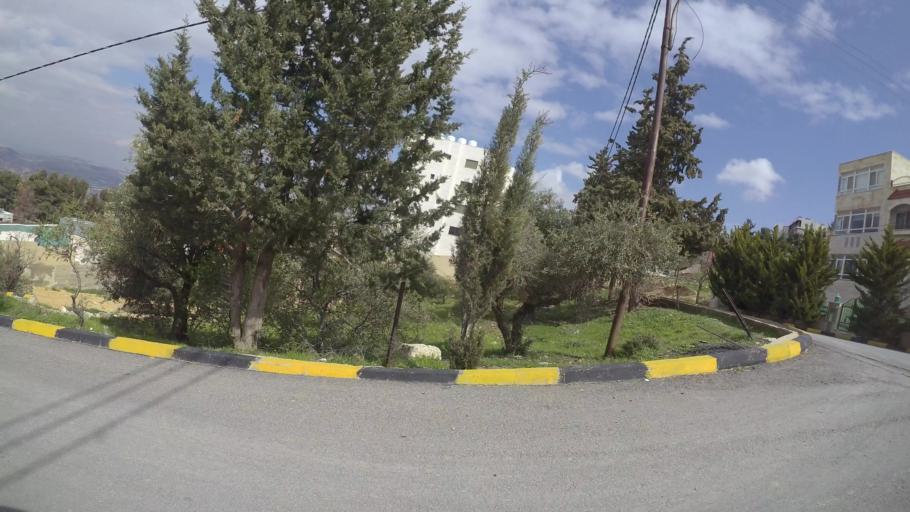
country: JO
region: Amman
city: Al Jubayhah
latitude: 32.0359
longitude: 35.8177
